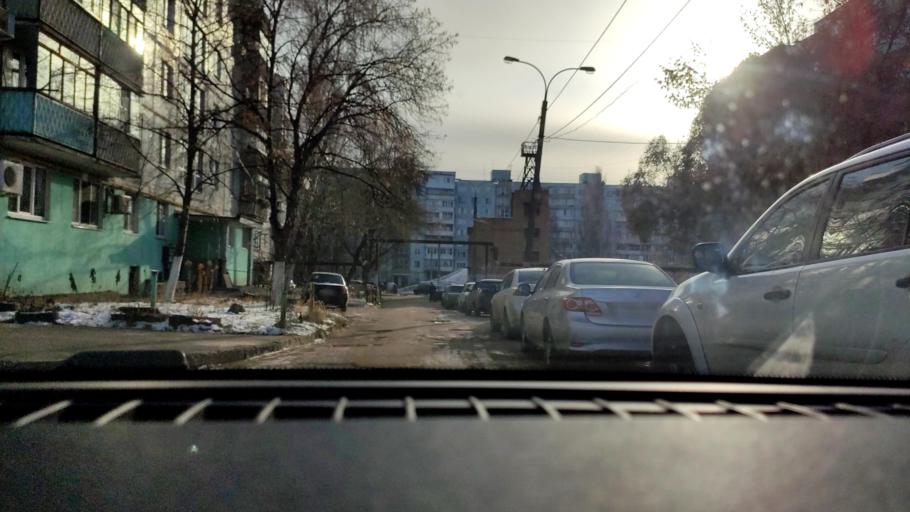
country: RU
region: Samara
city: Petra-Dubrava
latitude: 53.3021
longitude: 50.2780
